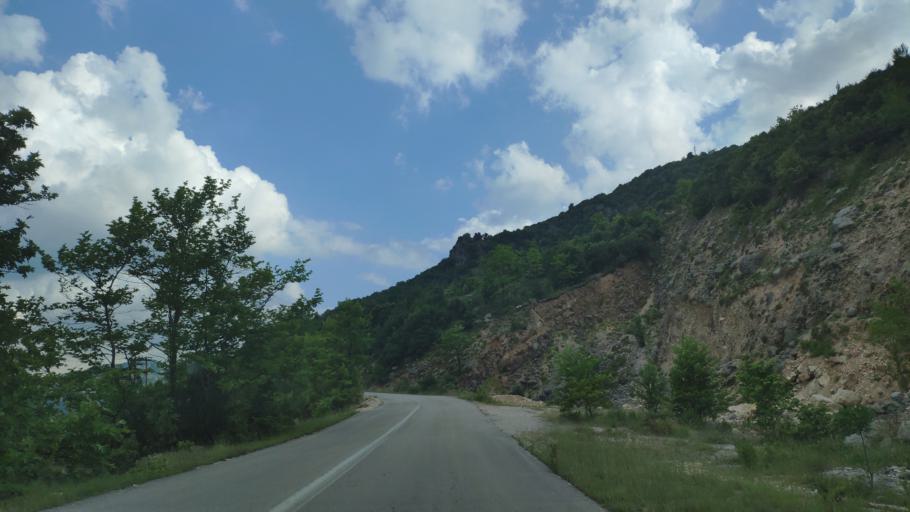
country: GR
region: Epirus
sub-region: Nomos Artas
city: Agios Dimitrios
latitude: 39.4659
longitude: 21.0218
